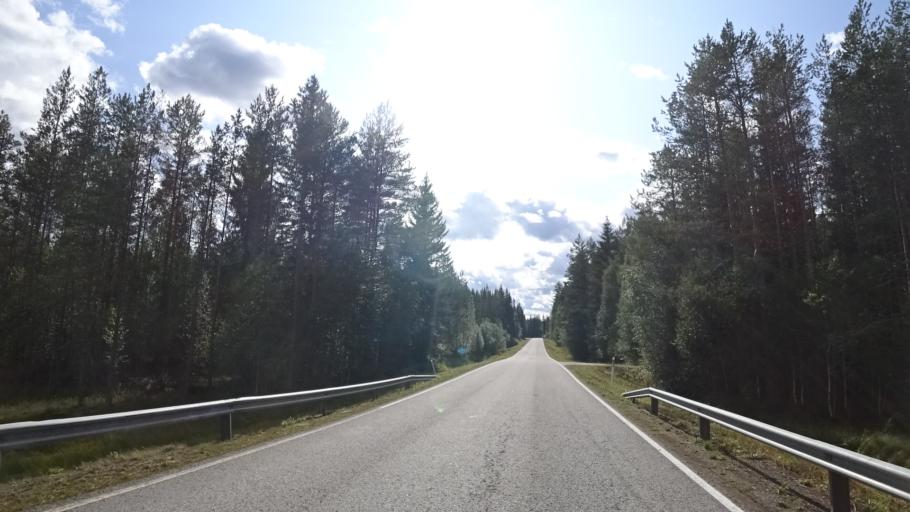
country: RU
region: Republic of Karelia
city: Vyartsilya
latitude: 62.2451
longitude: 30.7144
